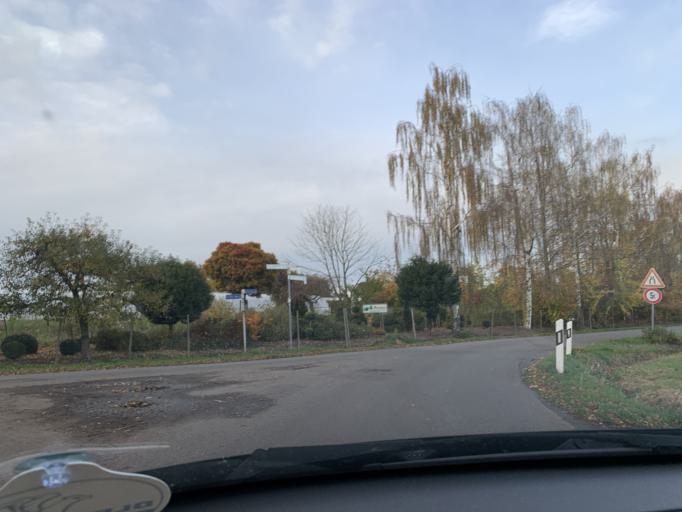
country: DE
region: Lower Saxony
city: Bad Zwischenahn
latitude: 53.2332
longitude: 8.0463
